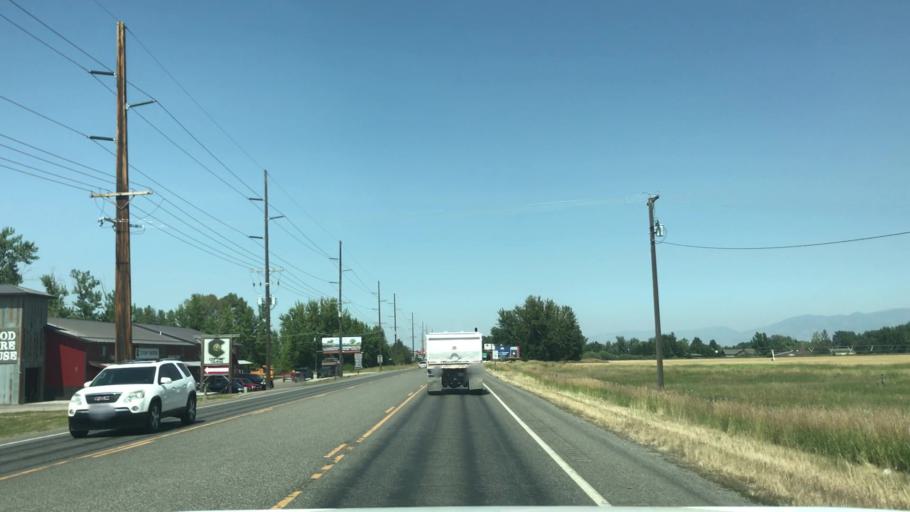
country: US
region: Montana
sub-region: Gallatin County
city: Four Corners
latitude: 45.6624
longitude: -111.1857
